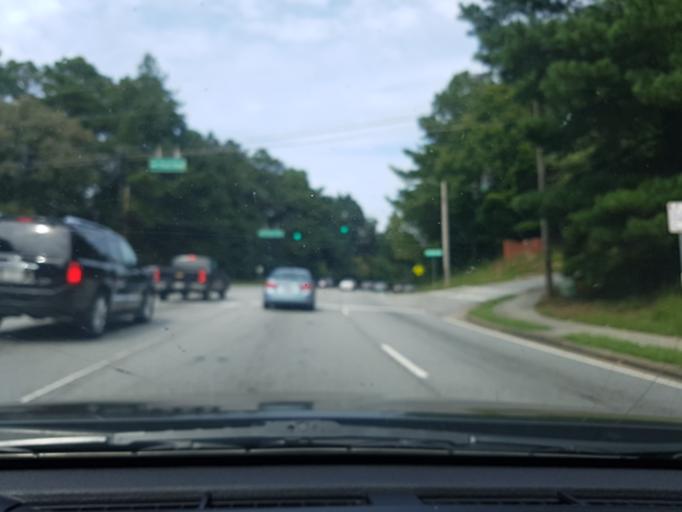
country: US
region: Georgia
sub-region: Gwinnett County
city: Norcross
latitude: 33.9398
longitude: -84.1678
